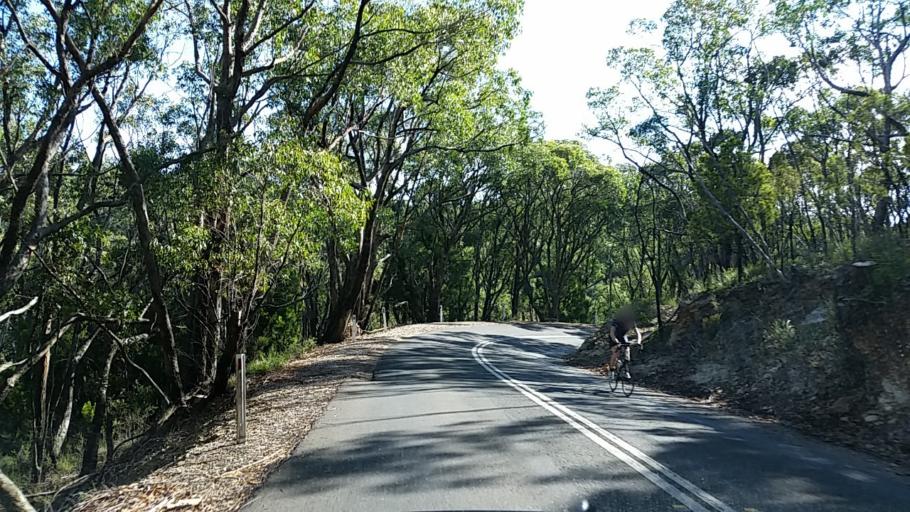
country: AU
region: South Australia
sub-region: Adelaide Hills
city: Crafers
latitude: -34.9651
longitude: 138.7128
